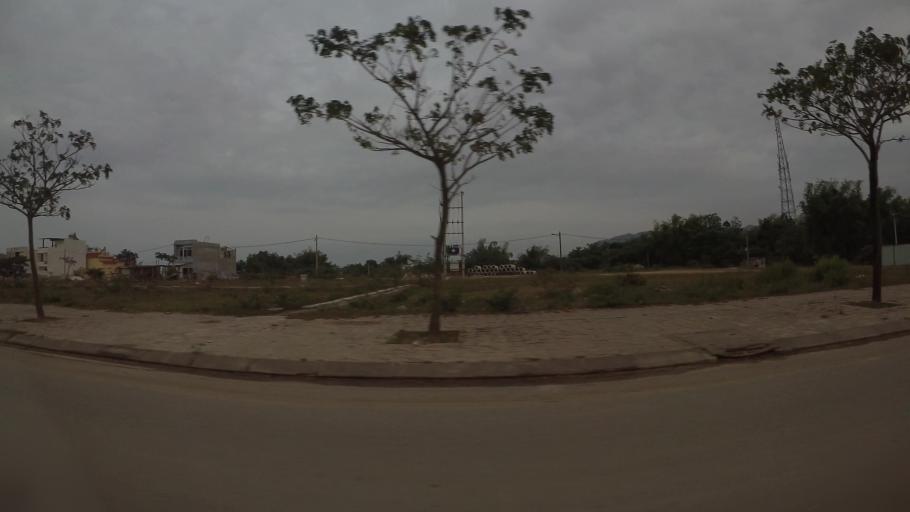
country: VN
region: Da Nang
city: Lien Chieu
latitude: 16.0968
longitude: 108.1134
